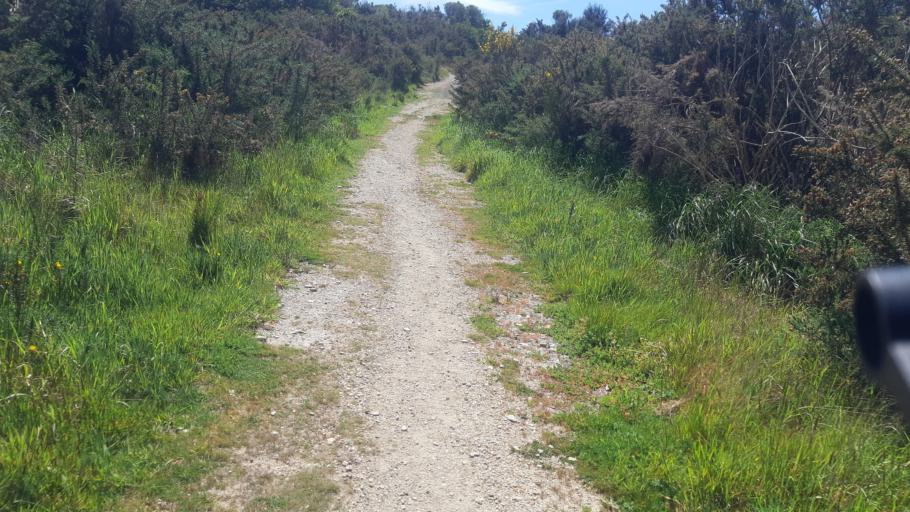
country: NZ
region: Marlborough
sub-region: Marlborough District
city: Picton
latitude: -41.2714
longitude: 174.0240
